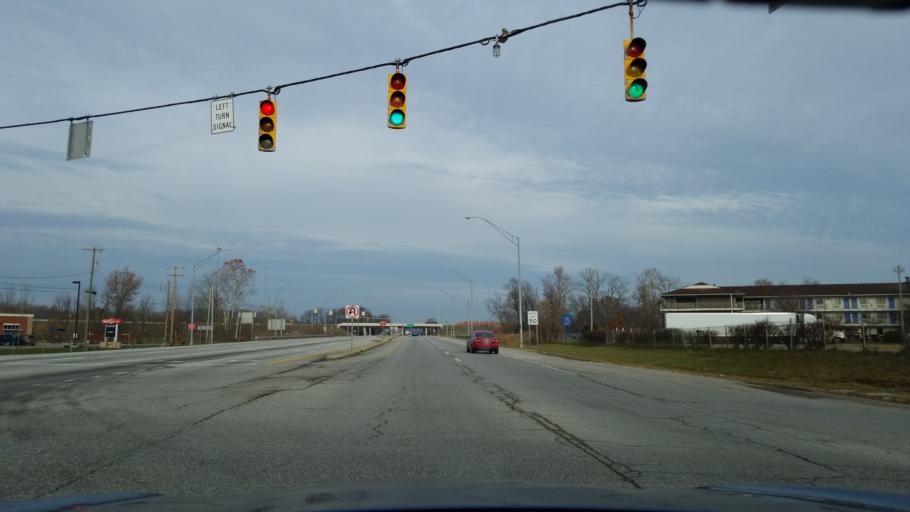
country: US
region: Ohio
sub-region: Summit County
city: Macedonia
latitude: 41.2992
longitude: -81.5149
